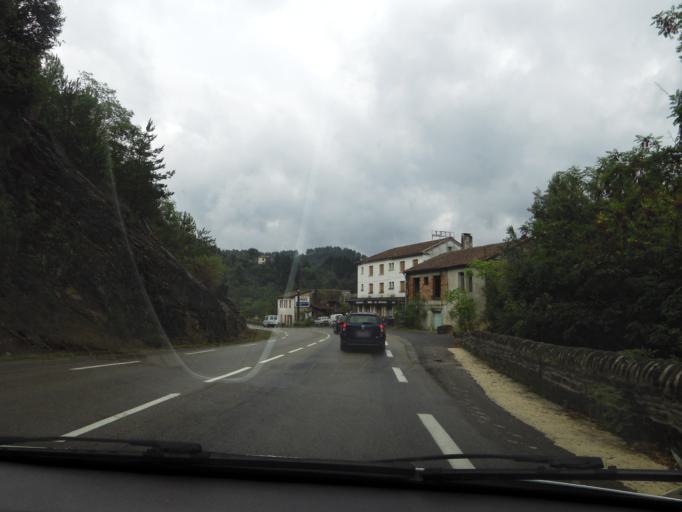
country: FR
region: Languedoc-Roussillon
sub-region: Departement du Gard
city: Branoux-les-Taillades
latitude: 44.2522
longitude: 3.9701
